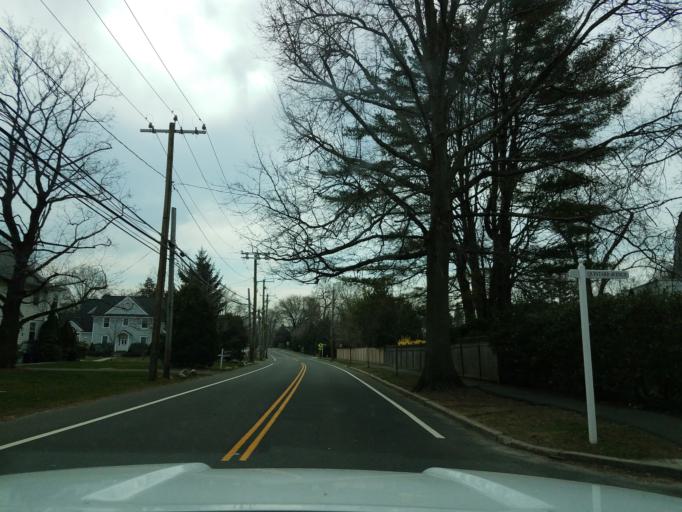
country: US
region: Connecticut
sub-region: Fairfield County
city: Old Greenwich
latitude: 41.0238
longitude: -73.5656
